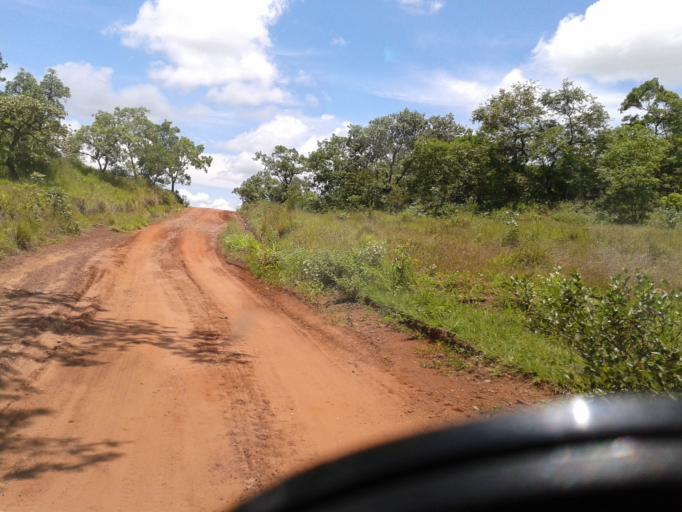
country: BR
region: Minas Gerais
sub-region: Santa Vitoria
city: Santa Vitoria
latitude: -18.9828
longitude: -49.8952
